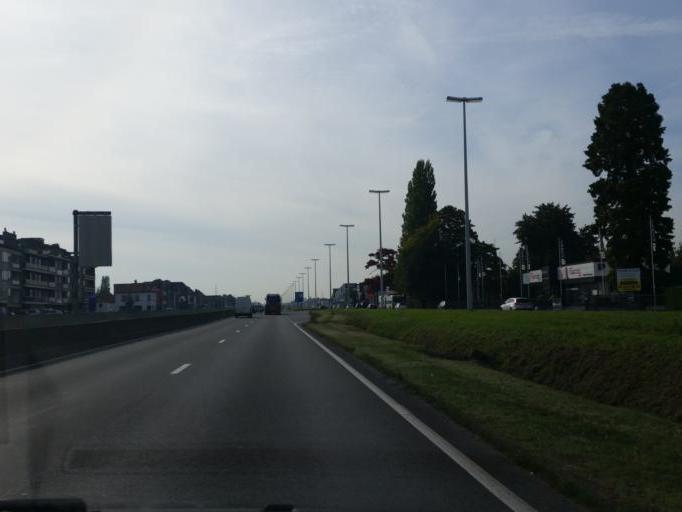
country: BE
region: Flanders
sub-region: Provincie Antwerpen
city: Aartselaar
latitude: 51.1416
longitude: 4.3790
